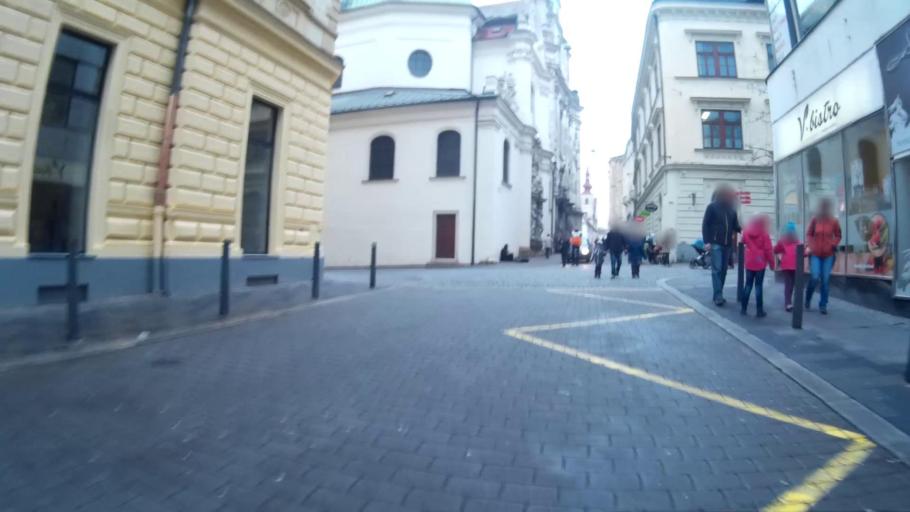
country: CZ
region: South Moravian
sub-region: Mesto Brno
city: Brno
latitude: 49.1948
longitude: 16.6103
